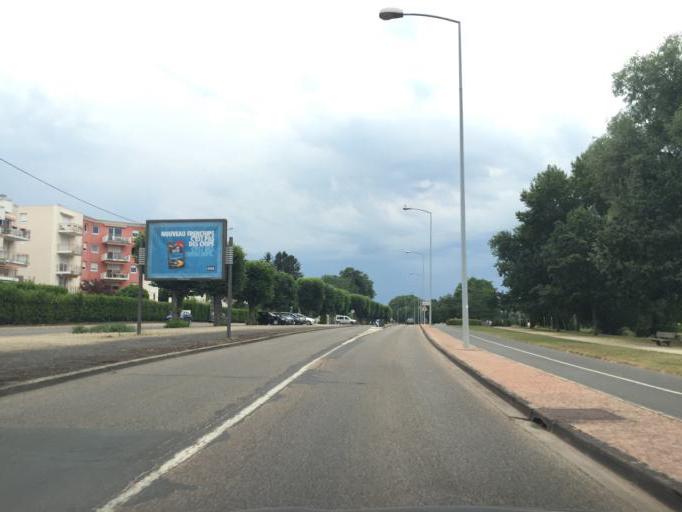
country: FR
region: Auvergne
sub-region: Departement de l'Allier
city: Moulins
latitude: 46.5532
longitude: 3.3311
